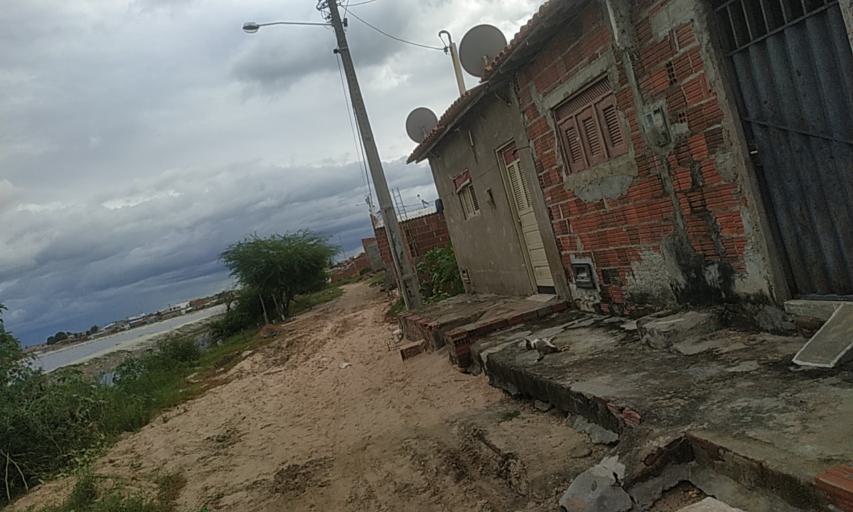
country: BR
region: Rio Grande do Norte
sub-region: Areia Branca
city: Areia Branca
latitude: -4.9560
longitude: -37.1266
